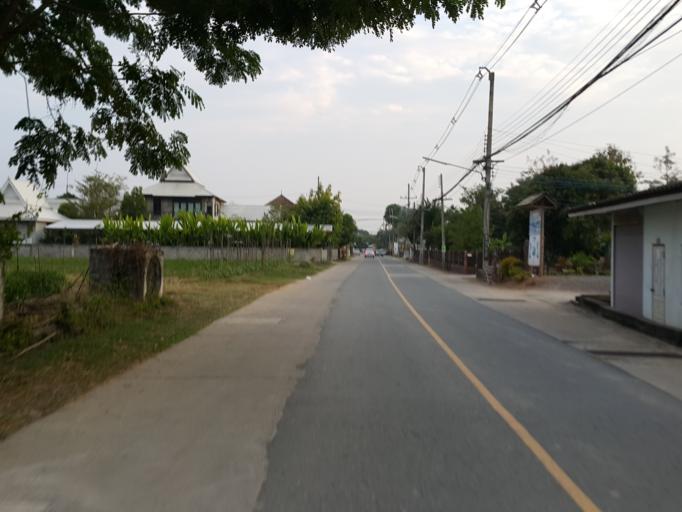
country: TH
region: Chiang Mai
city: San Sai
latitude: 18.8721
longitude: 99.1255
